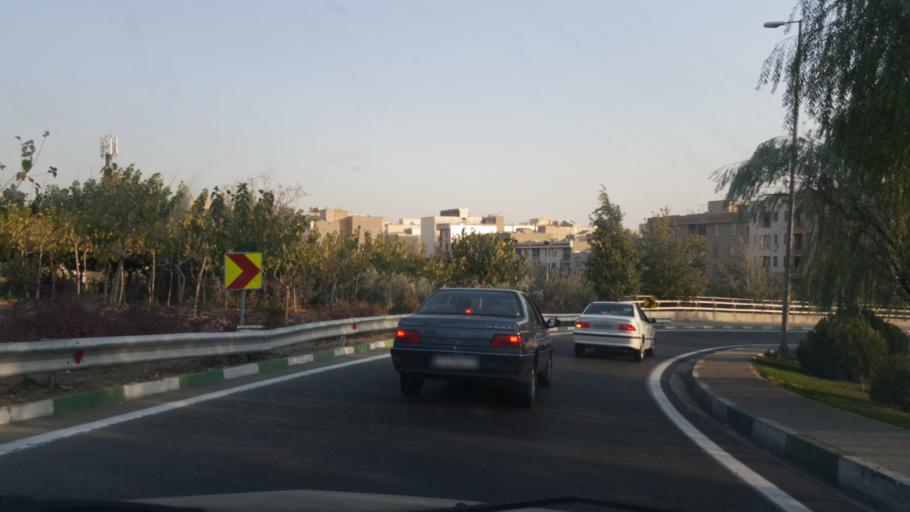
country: IR
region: Tehran
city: Tehran
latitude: 35.7330
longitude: 51.2961
